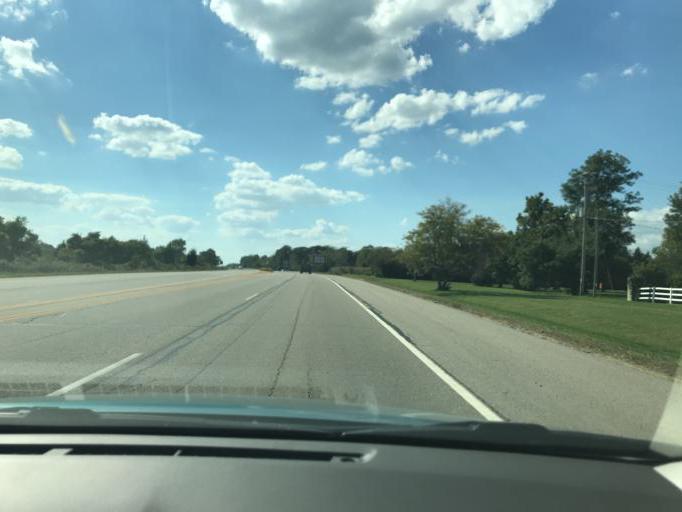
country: US
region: Wisconsin
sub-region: Walworth County
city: Lake Geneva
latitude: 42.5899
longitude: -88.4617
